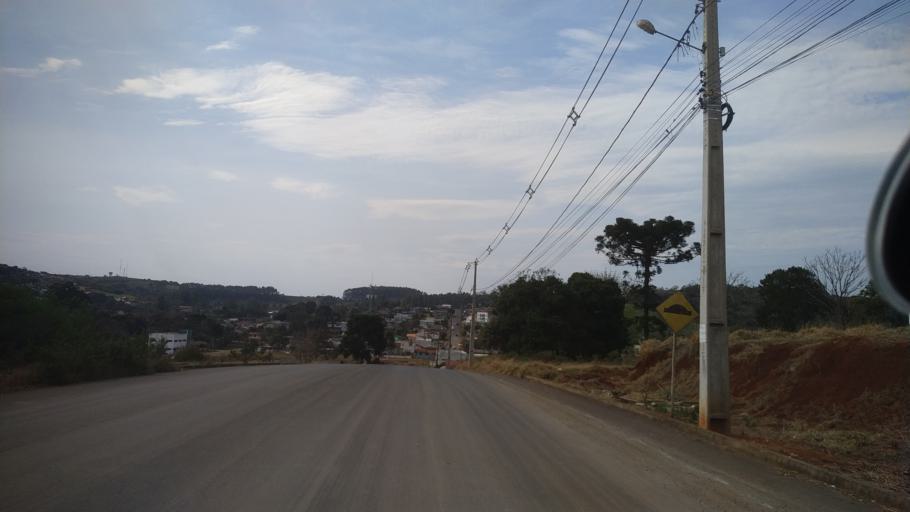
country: BR
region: Santa Catarina
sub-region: Chapeco
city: Chapeco
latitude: -27.1319
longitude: -52.6055
